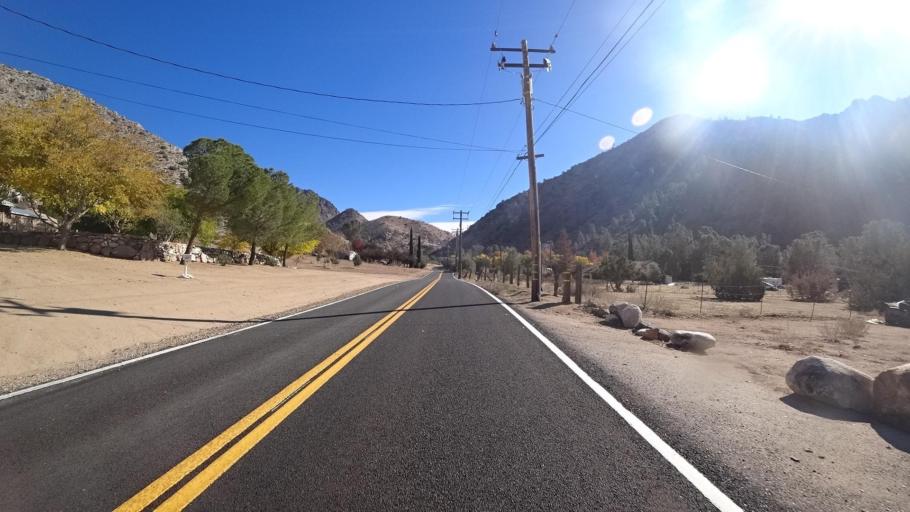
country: US
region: California
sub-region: Kern County
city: Lake Isabella
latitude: 35.5974
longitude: -118.4531
